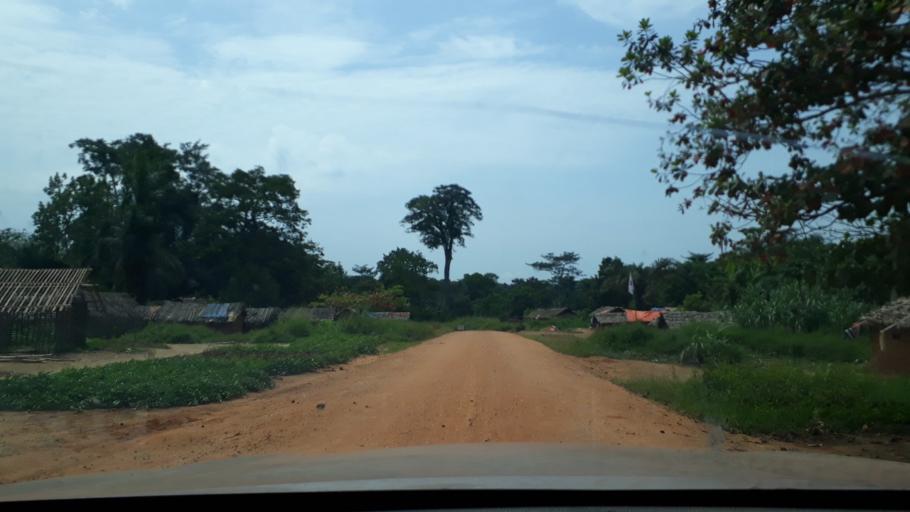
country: CD
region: Eastern Province
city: Wamba
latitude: 1.4047
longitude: 28.3944
